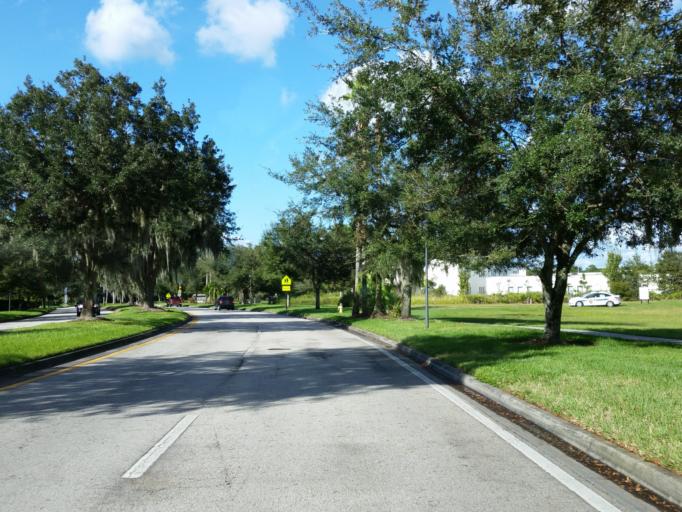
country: US
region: Florida
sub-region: Hillsborough County
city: Fish Hawk
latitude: 27.8473
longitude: -82.2324
